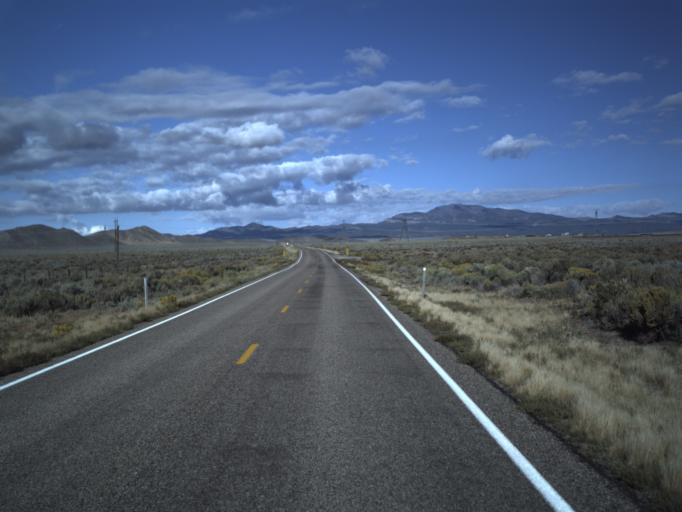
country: US
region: Utah
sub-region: Beaver County
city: Milford
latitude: 38.4062
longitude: -113.0498
